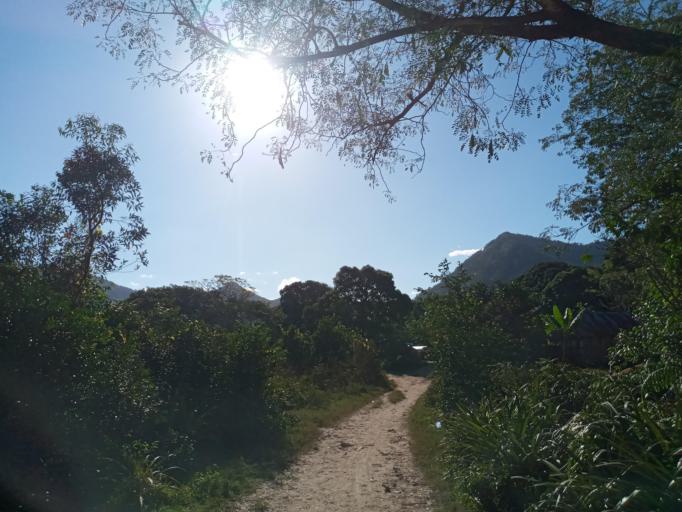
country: MG
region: Anosy
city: Fort Dauphin
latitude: -24.8259
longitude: 47.0447
